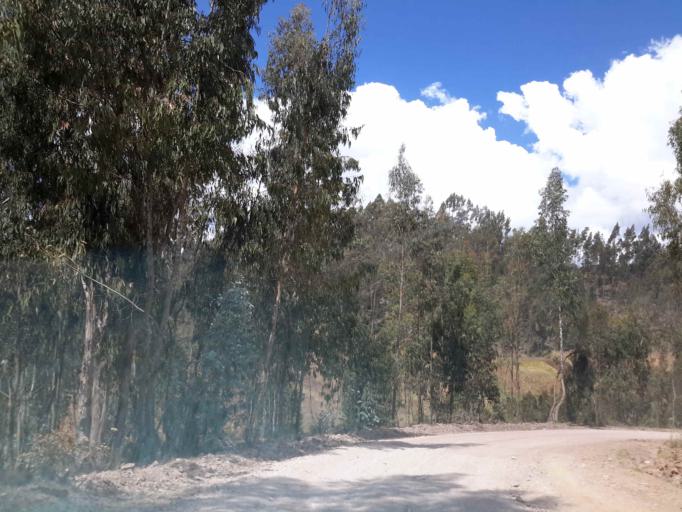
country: PE
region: Apurimac
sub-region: Provincia de Andahuaylas
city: Pacucha
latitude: -13.6214
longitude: -73.3349
